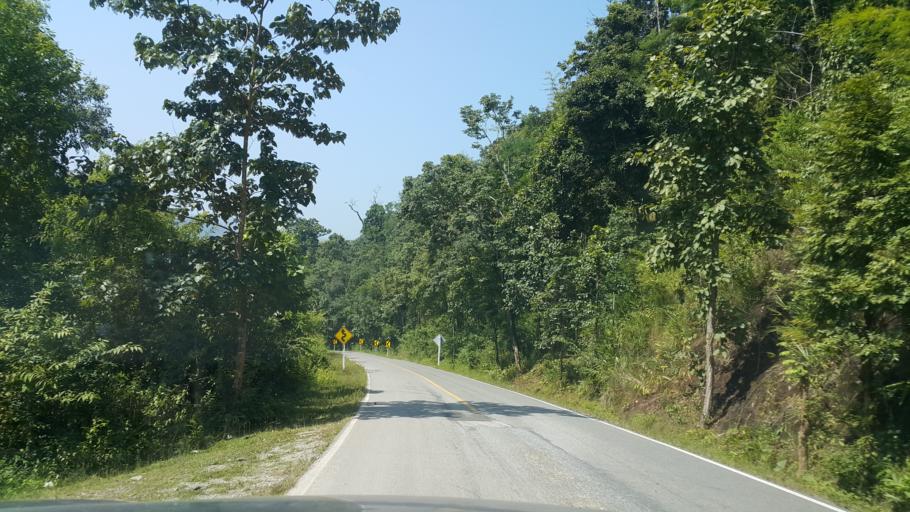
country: TH
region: Chiang Mai
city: Samoeng
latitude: 18.8590
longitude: 98.6570
